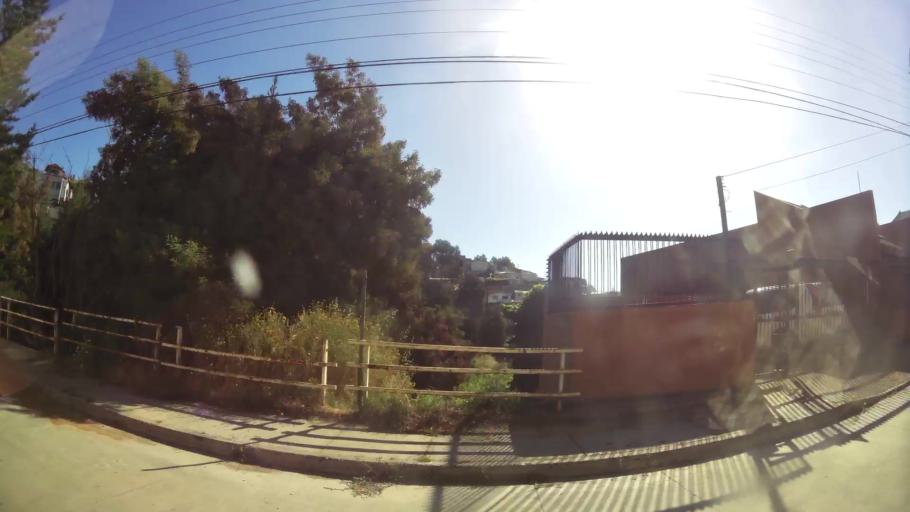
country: CL
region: Valparaiso
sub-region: Provincia de Valparaiso
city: Vina del Mar
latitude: -33.0371
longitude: -71.5579
